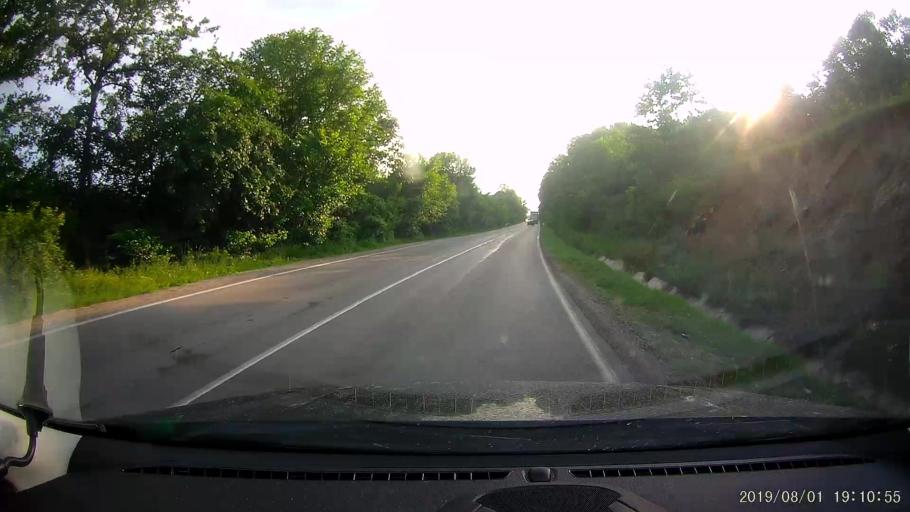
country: BG
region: Shumen
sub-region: Obshtina Smyadovo
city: Smyadovo
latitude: 42.9772
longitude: 26.9689
